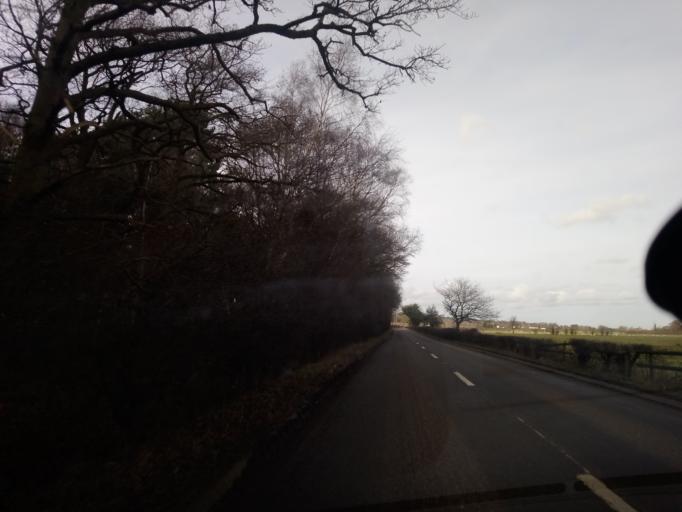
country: GB
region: England
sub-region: Shropshire
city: Stoke upon Tern
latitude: 52.8360
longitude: -2.5650
